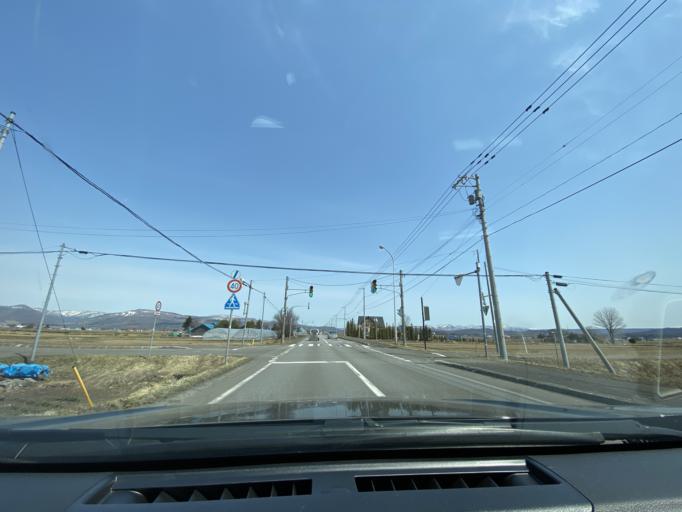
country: JP
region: Hokkaido
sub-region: Asahikawa-shi
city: Asahikawa
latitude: 43.8725
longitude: 142.4905
